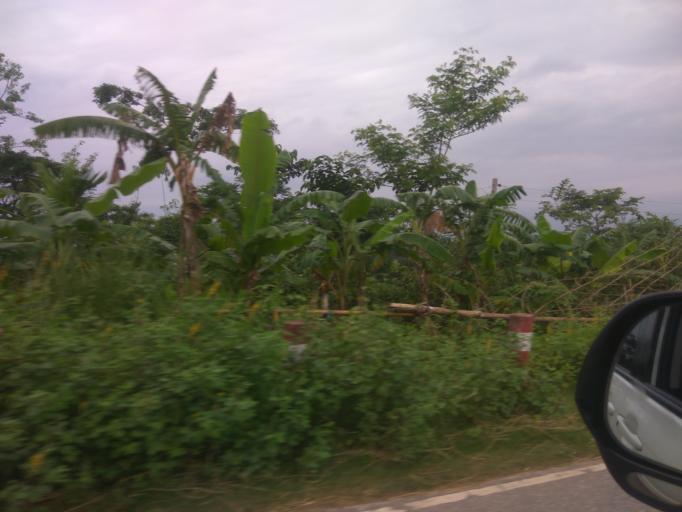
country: IN
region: Assam
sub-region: Karimganj
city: Karimganj
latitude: 24.9464
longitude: 92.2359
